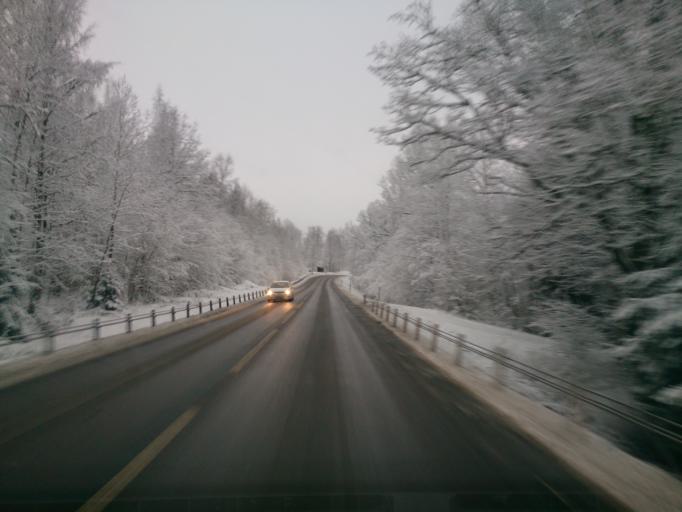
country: SE
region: OEstergoetland
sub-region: Atvidabergs Kommun
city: Atvidaberg
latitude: 58.2495
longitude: 15.9310
